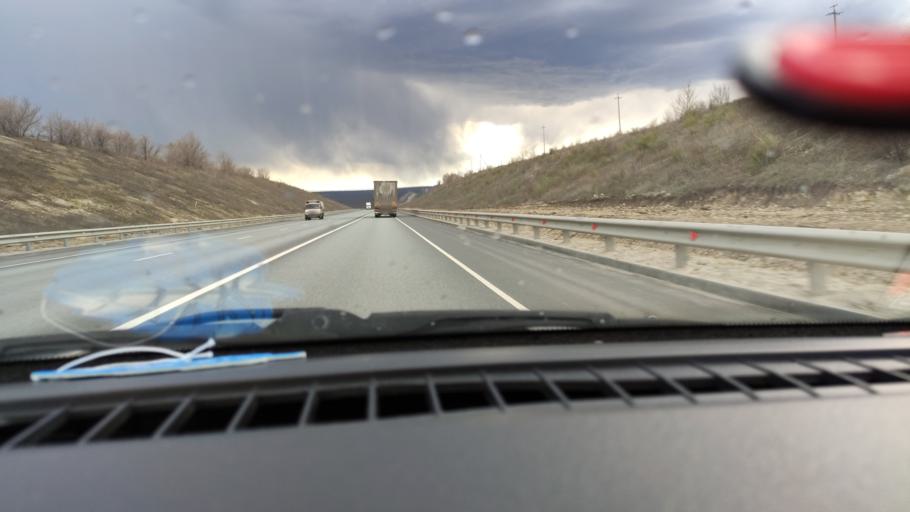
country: RU
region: Saratov
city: Yelshanka
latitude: 51.8862
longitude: 46.5170
